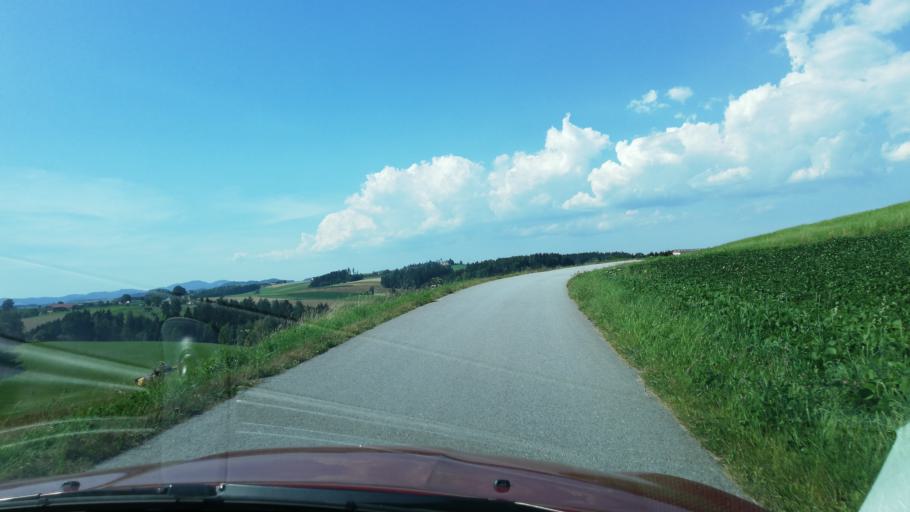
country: AT
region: Upper Austria
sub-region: Politischer Bezirk Rohrbach
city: Kleinzell im Muehlkreis
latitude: 48.4825
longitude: 14.0497
